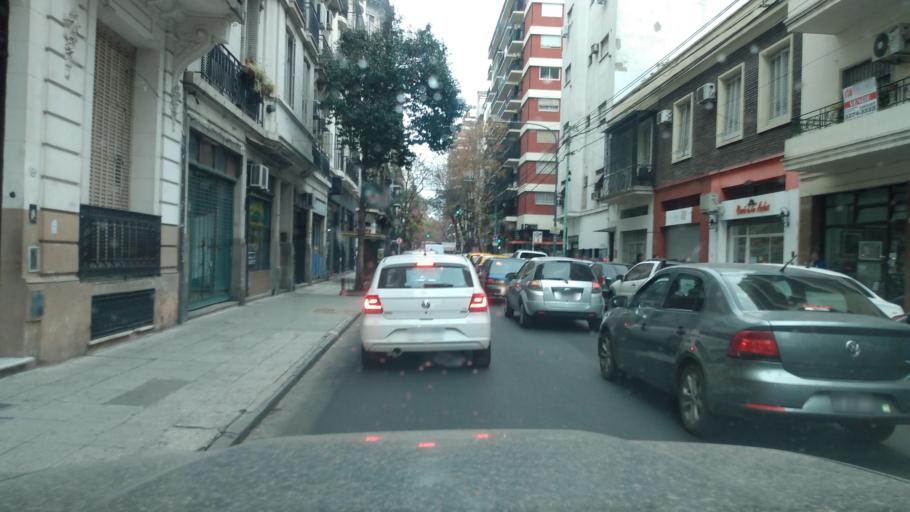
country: AR
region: Buenos Aires F.D.
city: Buenos Aires
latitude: -34.6078
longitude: -58.3964
